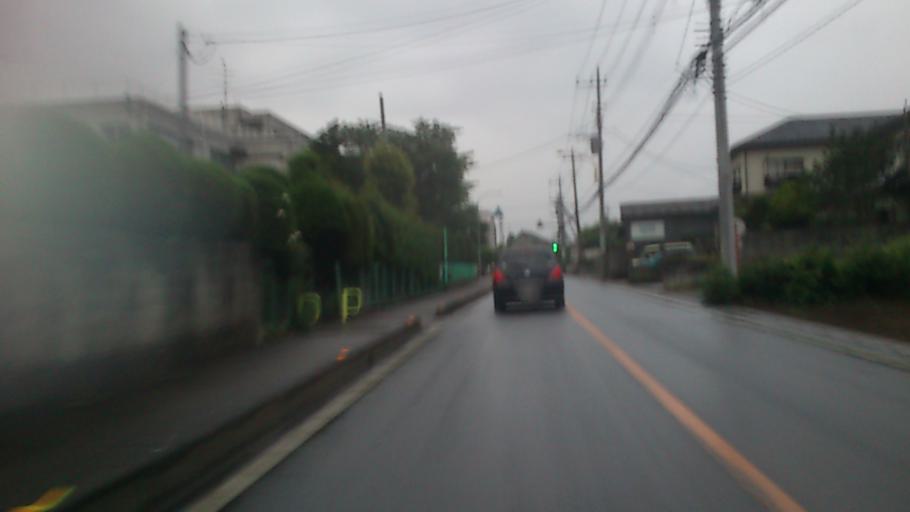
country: JP
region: Saitama
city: Kumagaya
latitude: 36.1542
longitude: 139.4072
